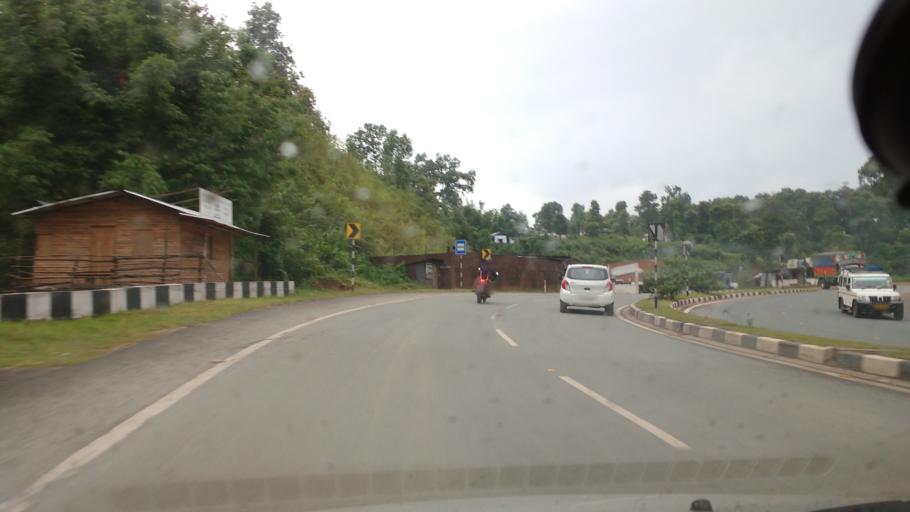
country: IN
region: Meghalaya
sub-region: Ri-Bhoi
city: Nongpoh
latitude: 25.7569
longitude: 91.8830
